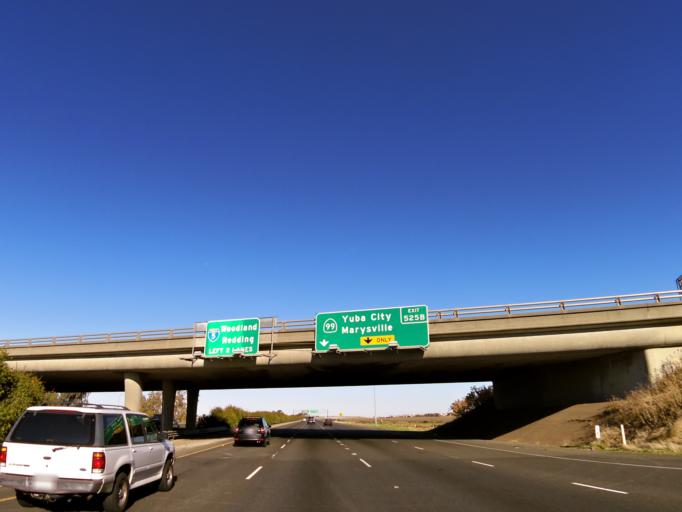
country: US
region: California
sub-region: Yolo County
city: West Sacramento
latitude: 38.6554
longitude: -121.5327
